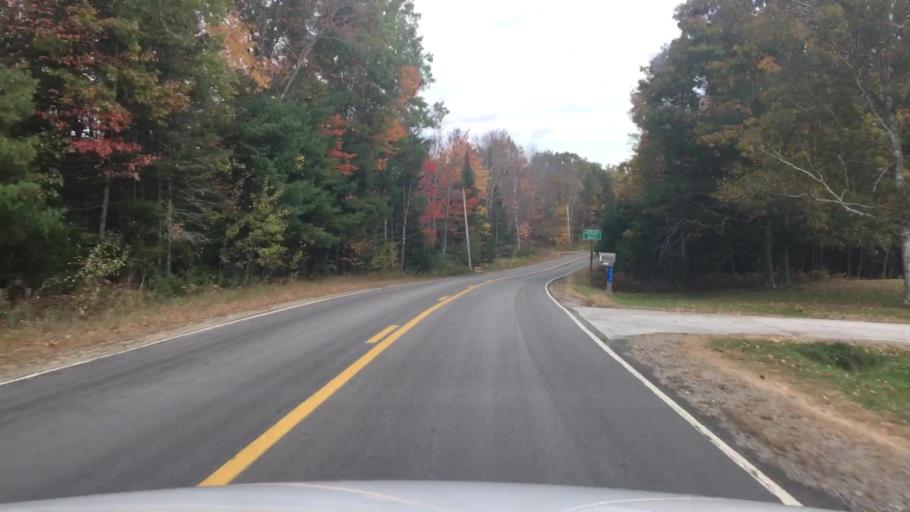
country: US
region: Maine
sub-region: Waldo County
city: Searsmont
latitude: 44.4042
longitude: -69.1376
